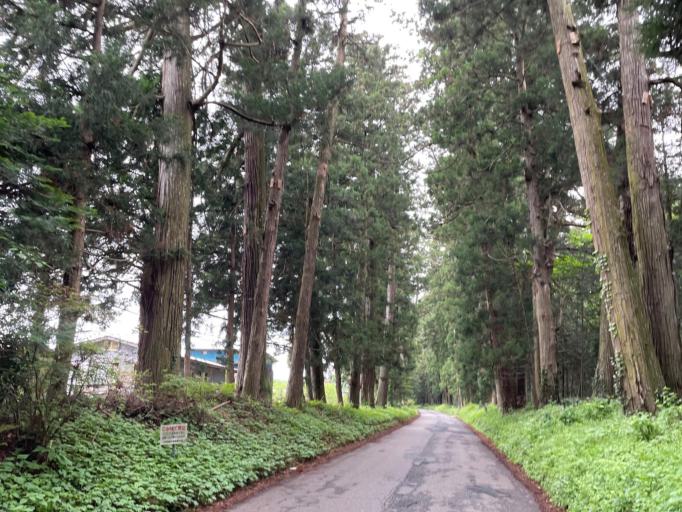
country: JP
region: Tochigi
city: Imaichi
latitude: 36.6922
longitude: 139.7627
